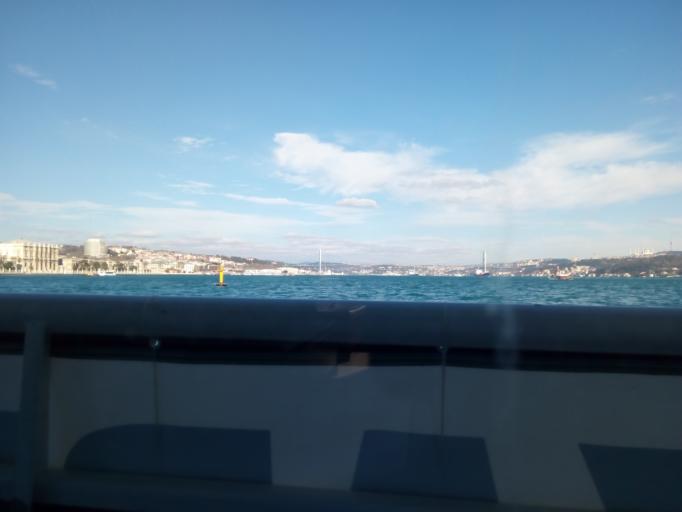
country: TR
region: Istanbul
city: Eminoenue
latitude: 41.0330
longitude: 28.9957
